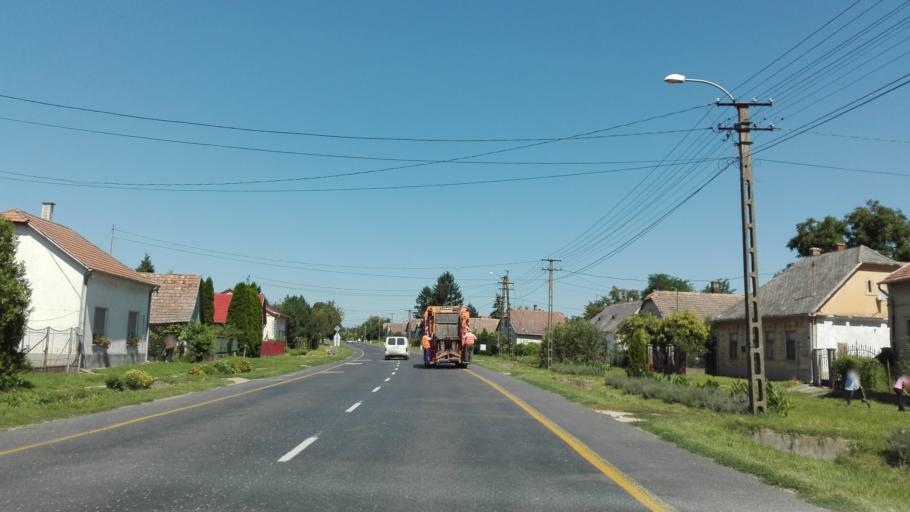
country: HU
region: Tolna
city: Simontornya
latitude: 46.7762
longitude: 18.5140
